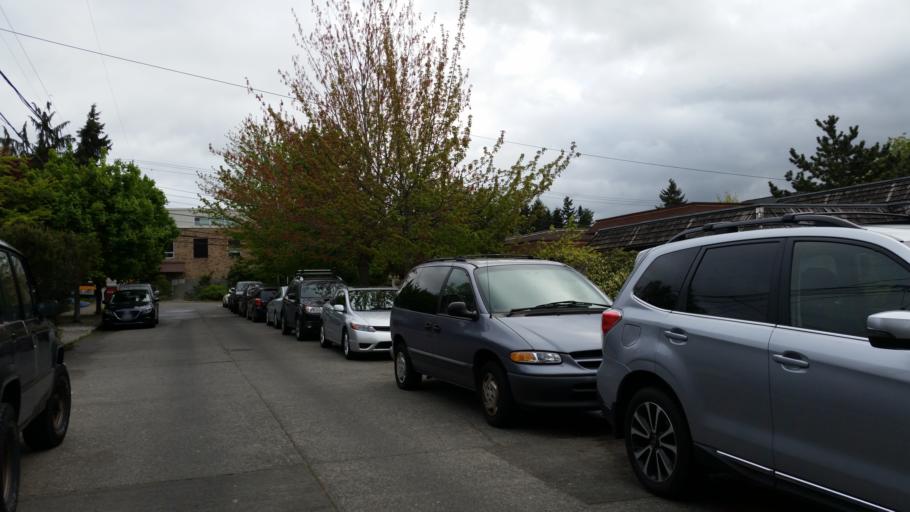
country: US
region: Washington
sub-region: King County
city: Shoreline
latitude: 47.6990
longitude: -122.3408
